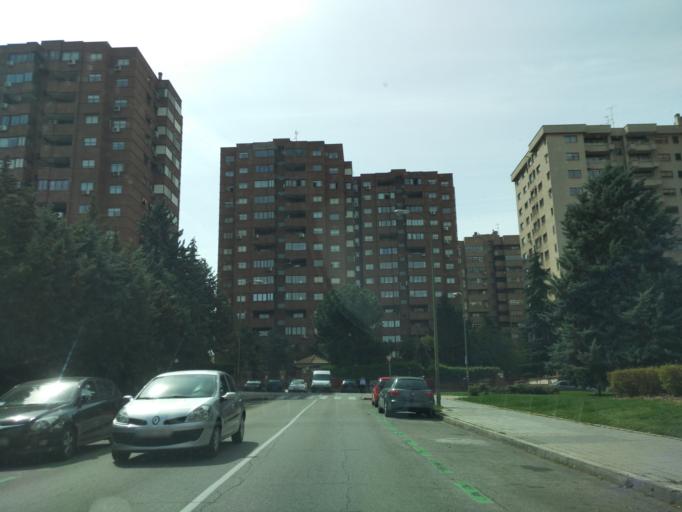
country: ES
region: Madrid
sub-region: Provincia de Madrid
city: Tetuan de las Victorias
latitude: 40.4784
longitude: -3.6969
